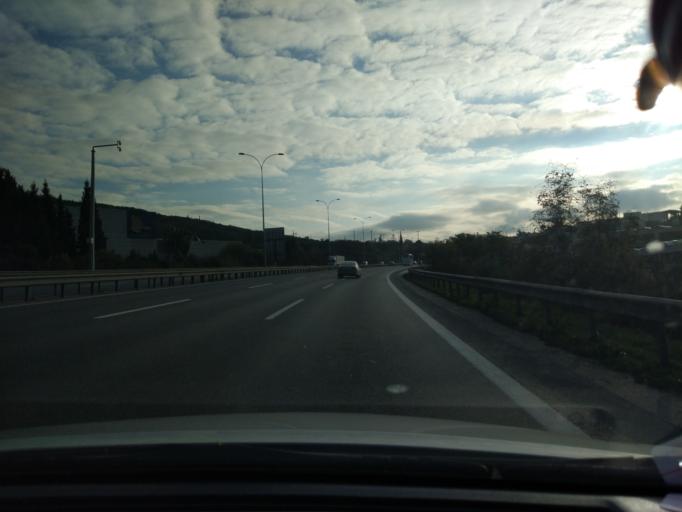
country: TR
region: Kocaeli
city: Tavsancil
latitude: 40.7762
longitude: 29.5440
